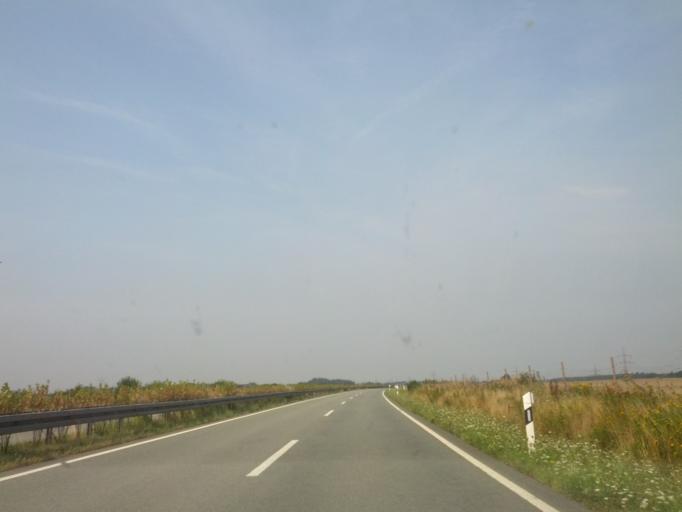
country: DE
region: Mecklenburg-Vorpommern
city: Brandshagen
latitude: 54.1870
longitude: 13.1641
